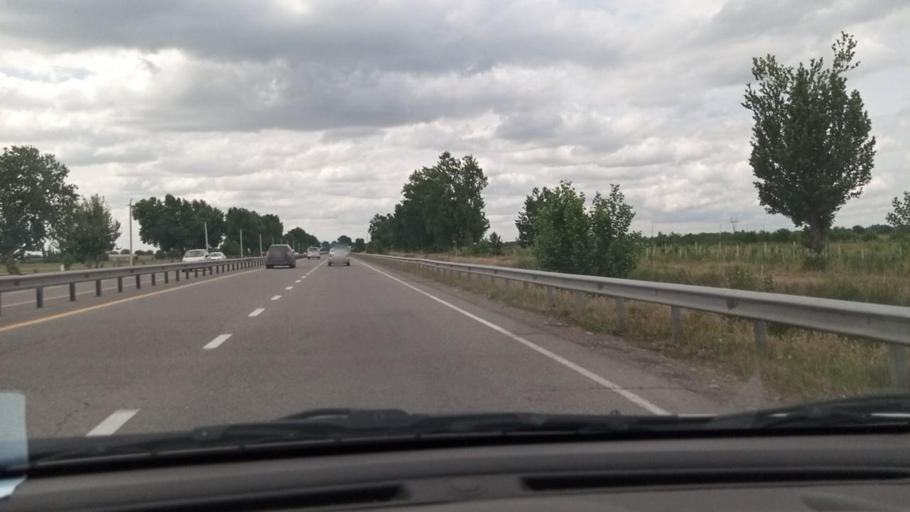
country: UZ
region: Toshkent Shahri
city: Bektemir
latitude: 41.1746
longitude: 69.4114
